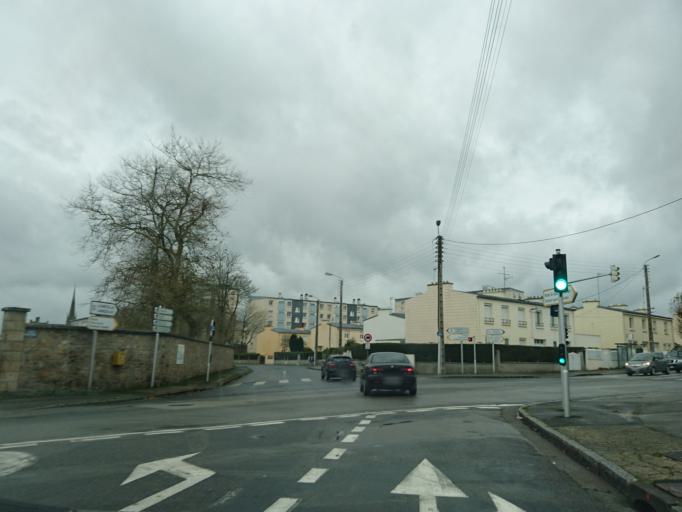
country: FR
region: Brittany
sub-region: Departement du Finistere
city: Brest
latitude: 48.4151
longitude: -4.4866
